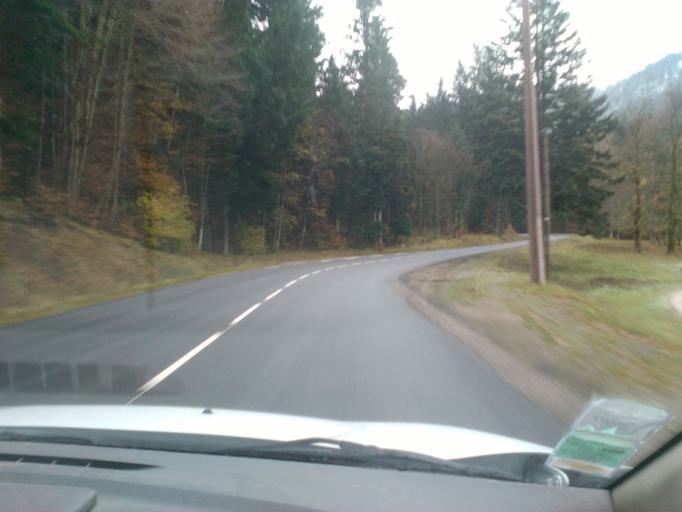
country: FR
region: Lorraine
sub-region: Departement des Vosges
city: Xonrupt-Longemer
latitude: 48.0564
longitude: 6.9872
